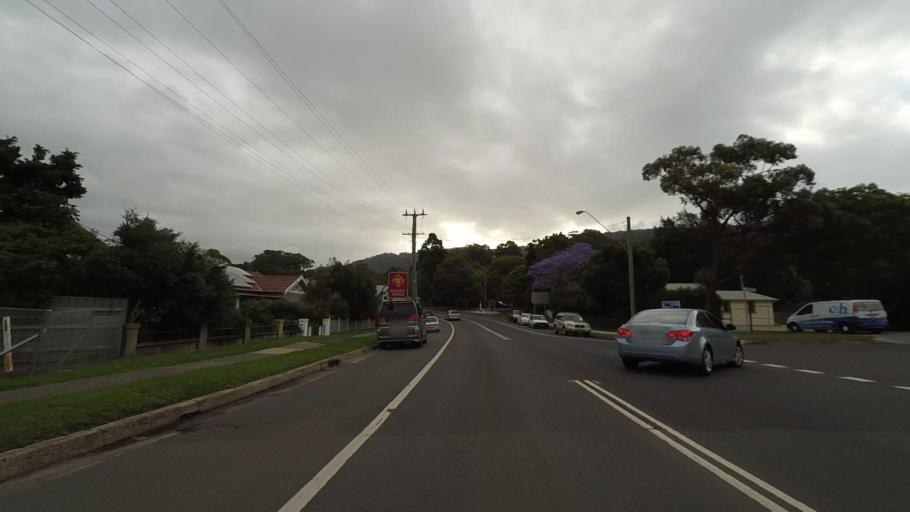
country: AU
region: New South Wales
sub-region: Wollongong
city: Bulli
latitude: -34.3199
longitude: 150.9150
